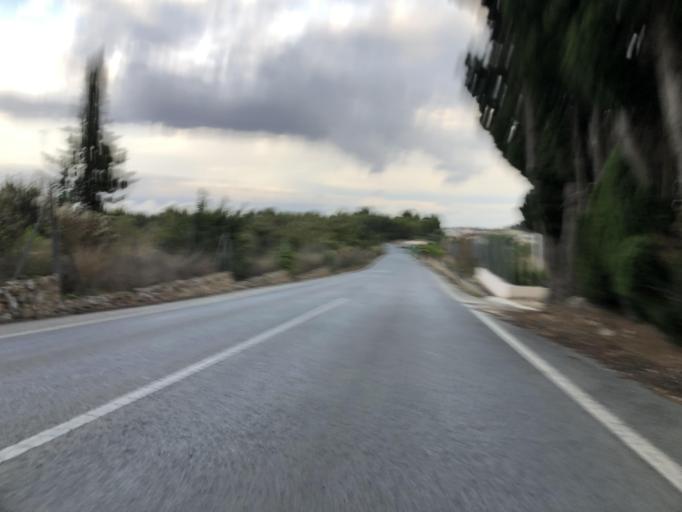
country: ES
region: Valencia
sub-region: Provincia de Alicante
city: Polop
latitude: 38.6270
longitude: -0.1389
